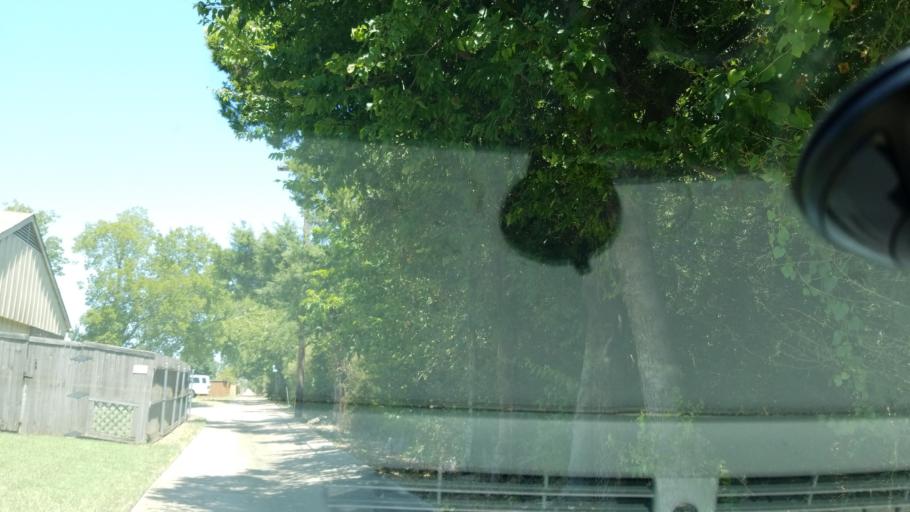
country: US
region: Texas
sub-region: Dallas County
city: Duncanville
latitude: 32.6367
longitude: -96.8837
